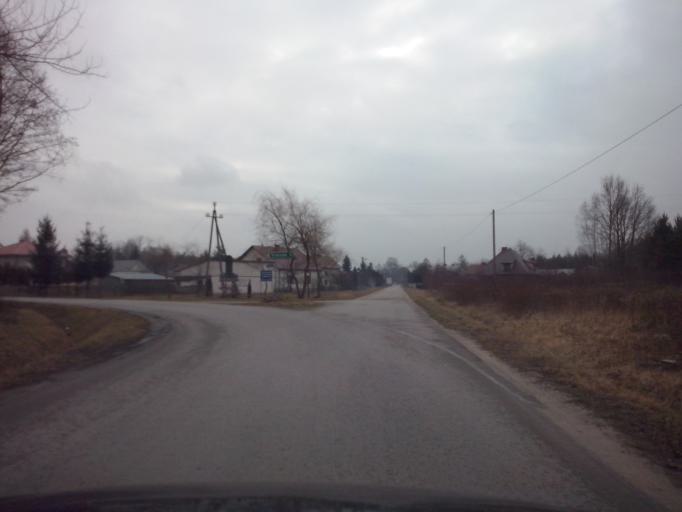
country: PL
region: Subcarpathian Voivodeship
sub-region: Powiat nizanski
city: Bieliny
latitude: 50.4510
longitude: 22.2860
